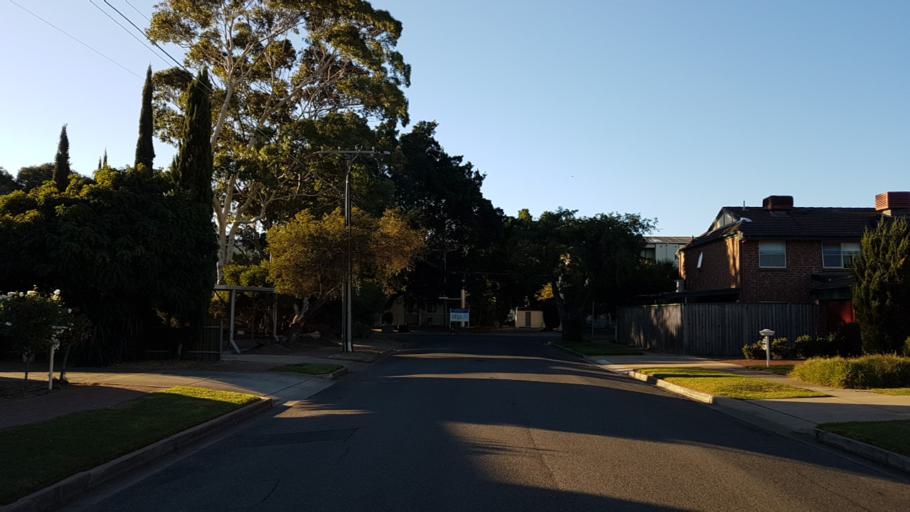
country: AU
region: South Australia
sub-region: Charles Sturt
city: Henley Beach
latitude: -34.9285
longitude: 138.5066
